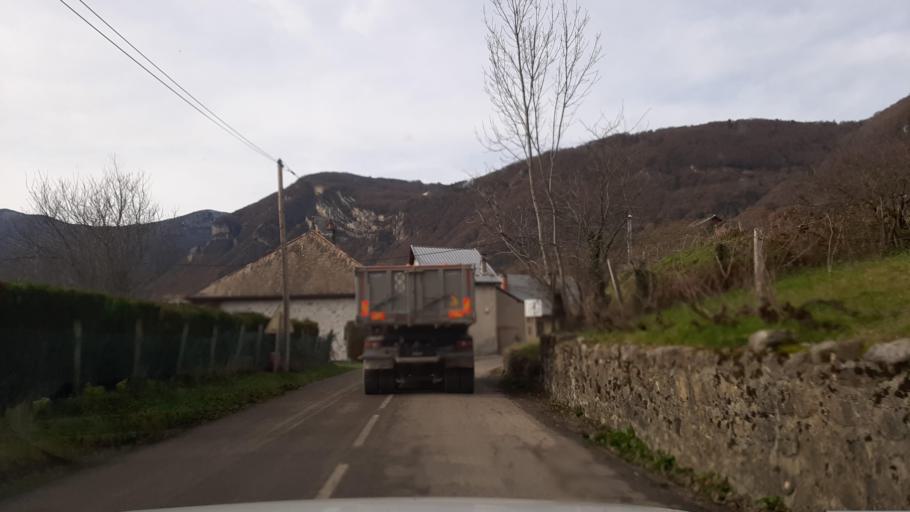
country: FR
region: Rhone-Alpes
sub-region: Departement de la Savoie
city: Coise-Saint-Jean-Pied-Gauthier
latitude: 45.5746
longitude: 6.1563
